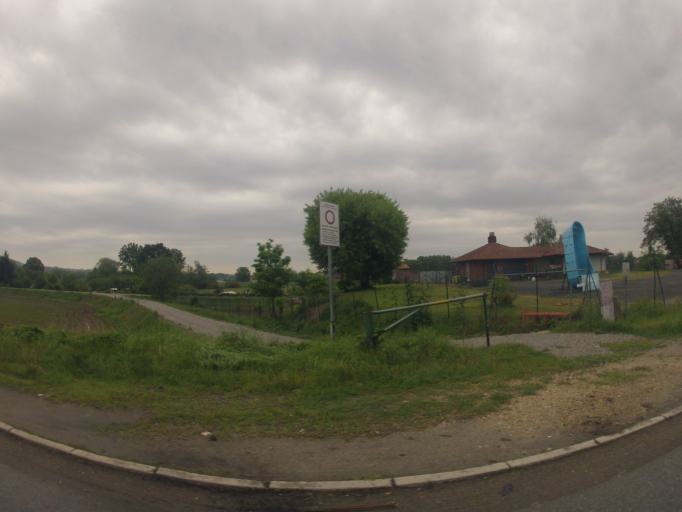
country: IT
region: Piedmont
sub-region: Provincia di Torino
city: Tagliaferro
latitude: 44.9754
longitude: 7.6702
